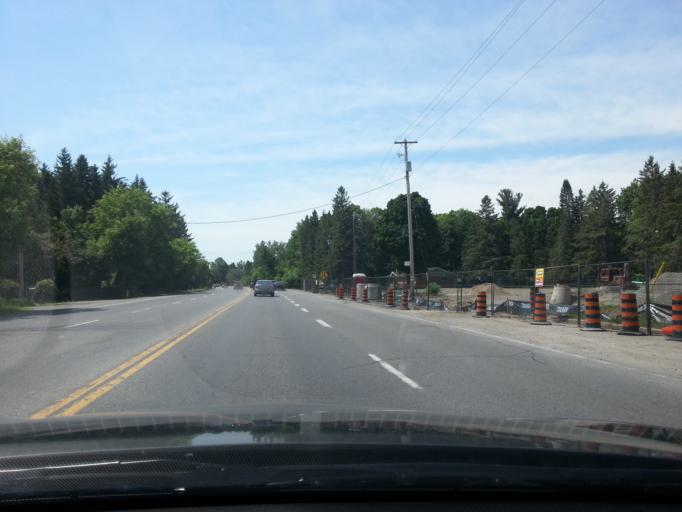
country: CA
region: Ontario
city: Ottawa
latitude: 45.3306
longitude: -75.7016
